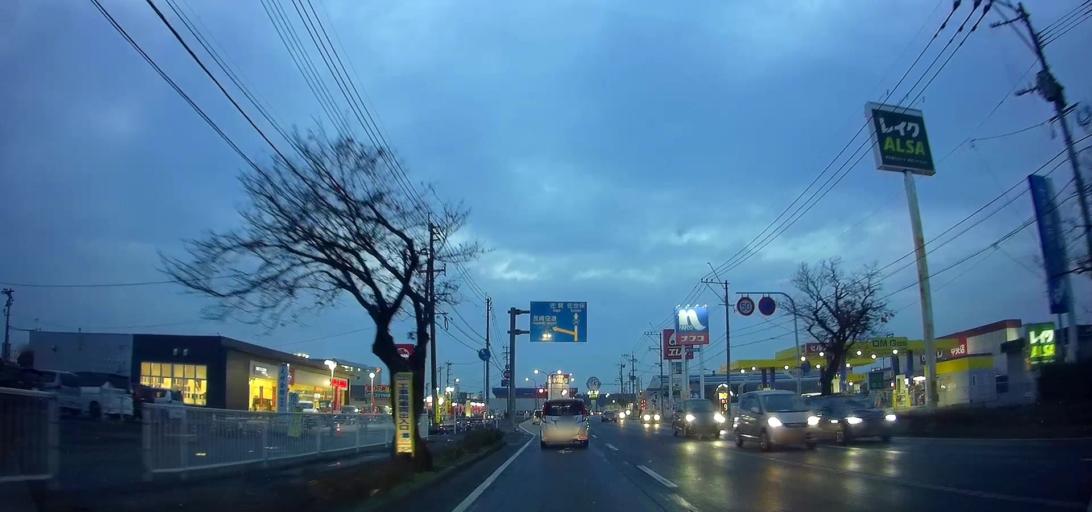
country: JP
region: Nagasaki
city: Omura
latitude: 32.9109
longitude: 129.9523
